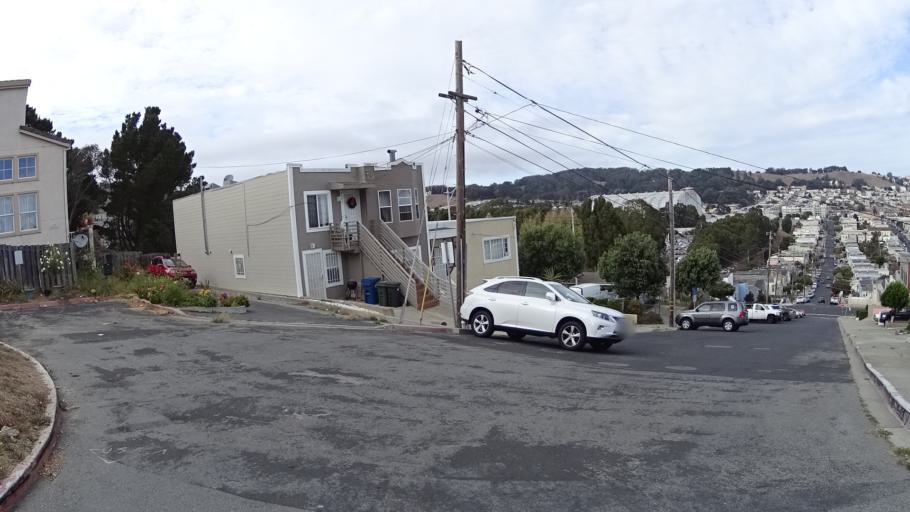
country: US
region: California
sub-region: San Mateo County
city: Brisbane
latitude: 37.7009
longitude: -122.4185
